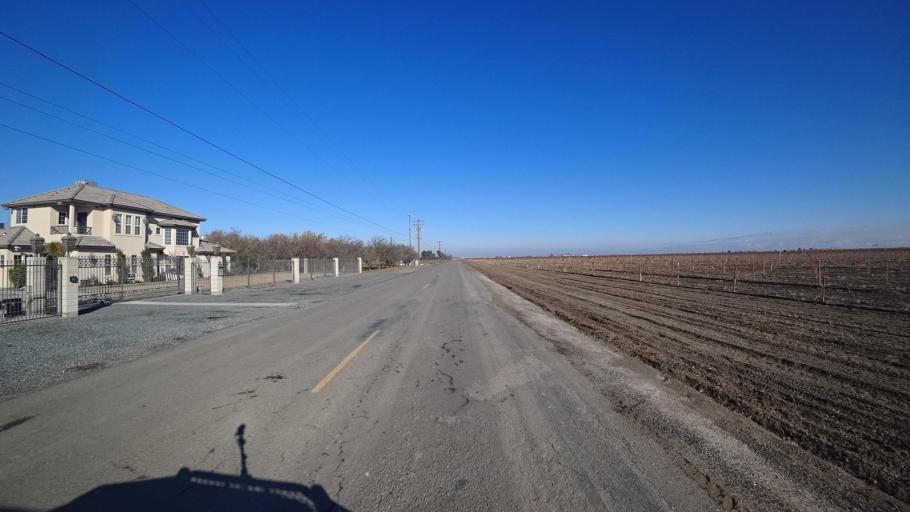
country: US
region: California
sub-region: Kern County
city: Delano
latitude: 35.7470
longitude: -119.3119
